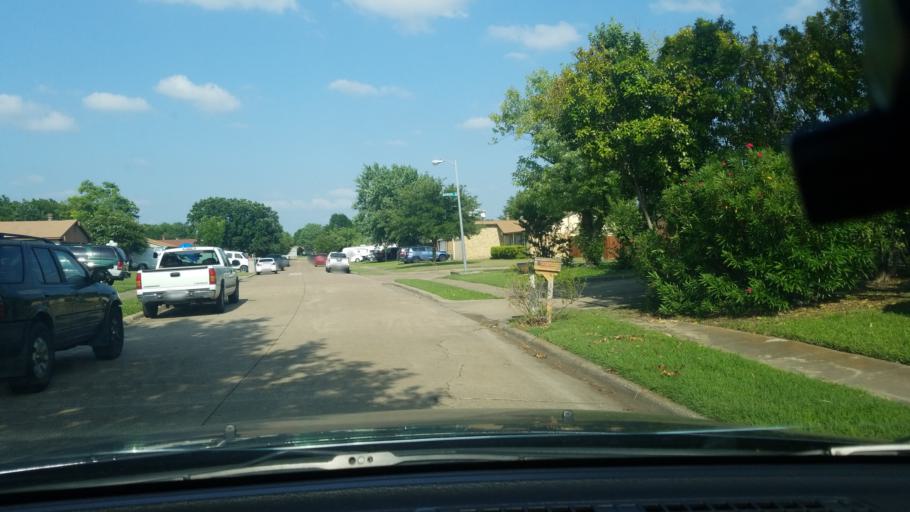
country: US
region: Texas
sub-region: Dallas County
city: Sunnyvale
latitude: 32.8160
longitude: -96.6008
